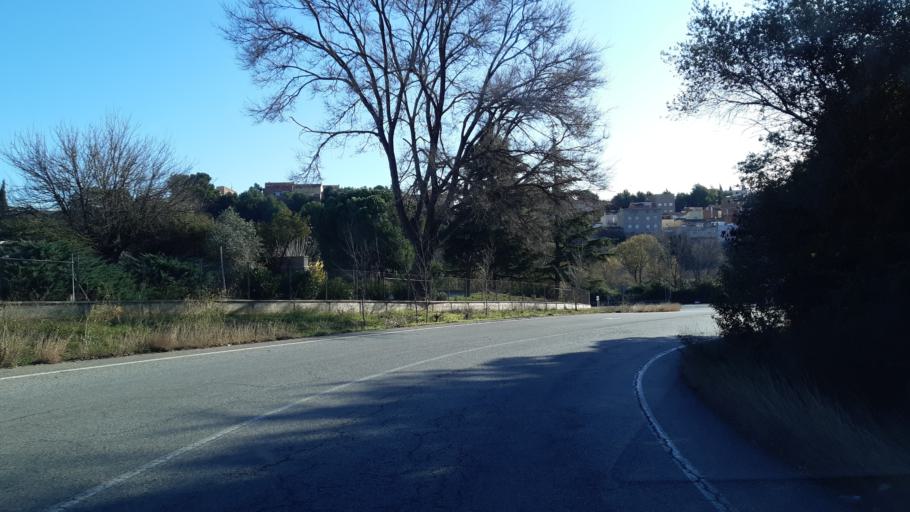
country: ES
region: Catalonia
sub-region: Provincia de Barcelona
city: Vilanova del Cami
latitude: 41.5836
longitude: 1.6348
